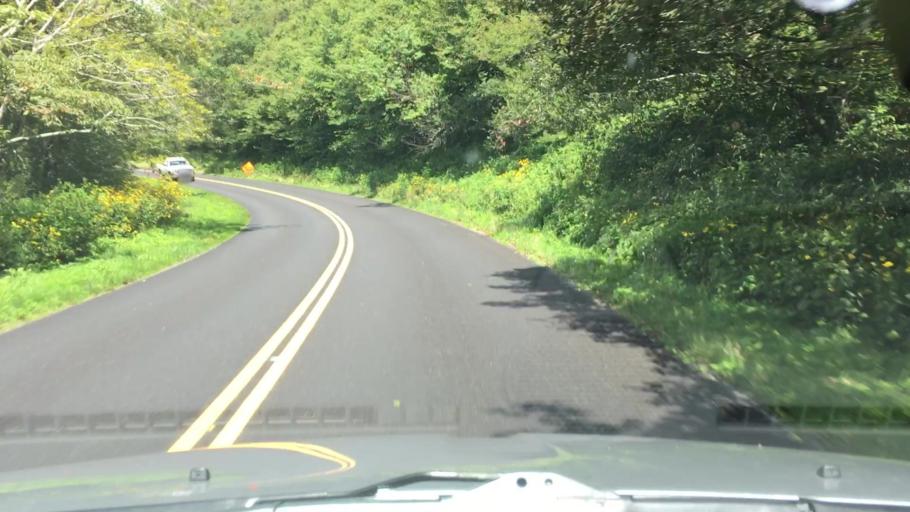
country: US
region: North Carolina
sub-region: Buncombe County
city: Black Mountain
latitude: 35.7391
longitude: -82.3409
